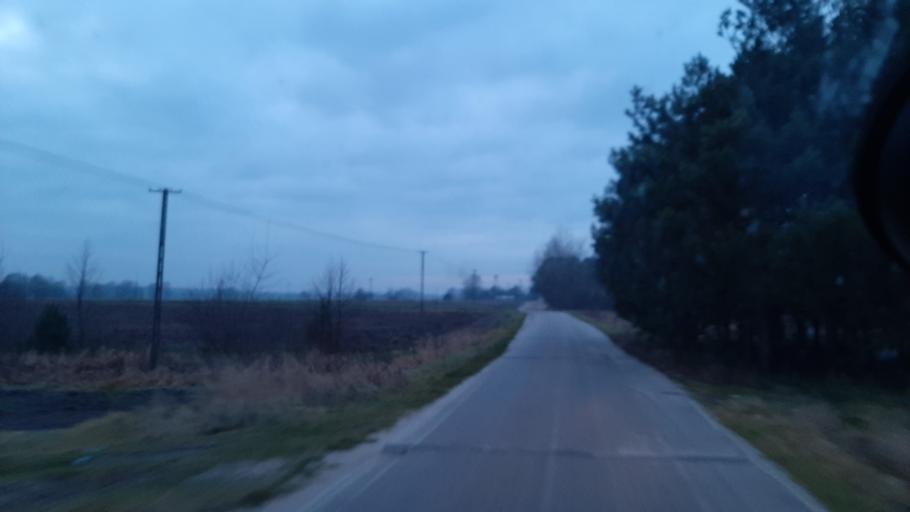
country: PL
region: Lublin Voivodeship
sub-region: Powiat lubartowski
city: Firlej
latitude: 51.5877
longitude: 22.5388
